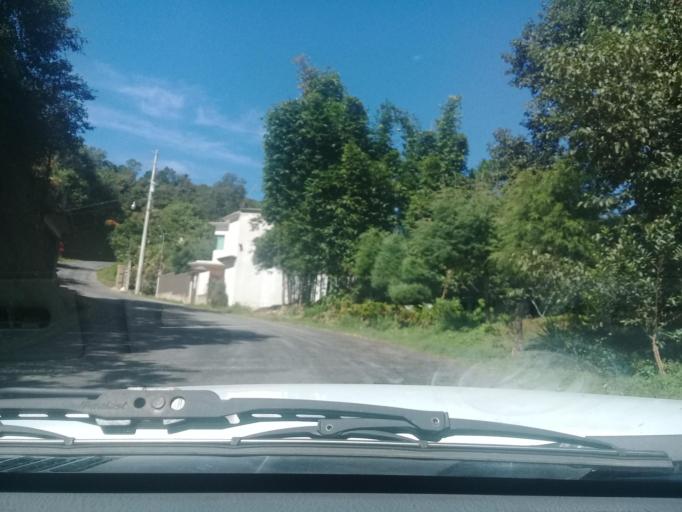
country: MX
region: Veracruz
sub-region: Tlalnelhuayocan
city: Otilpan
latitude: 19.5671
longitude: -96.9863
